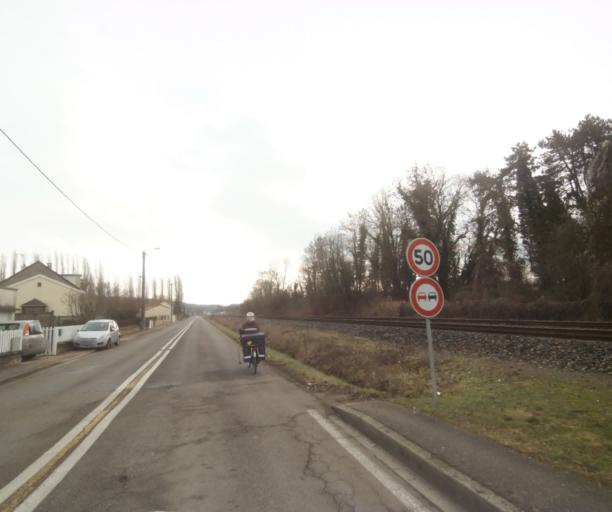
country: FR
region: Champagne-Ardenne
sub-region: Departement de la Haute-Marne
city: Bettancourt-la-Ferree
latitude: 48.6355
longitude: 4.9731
